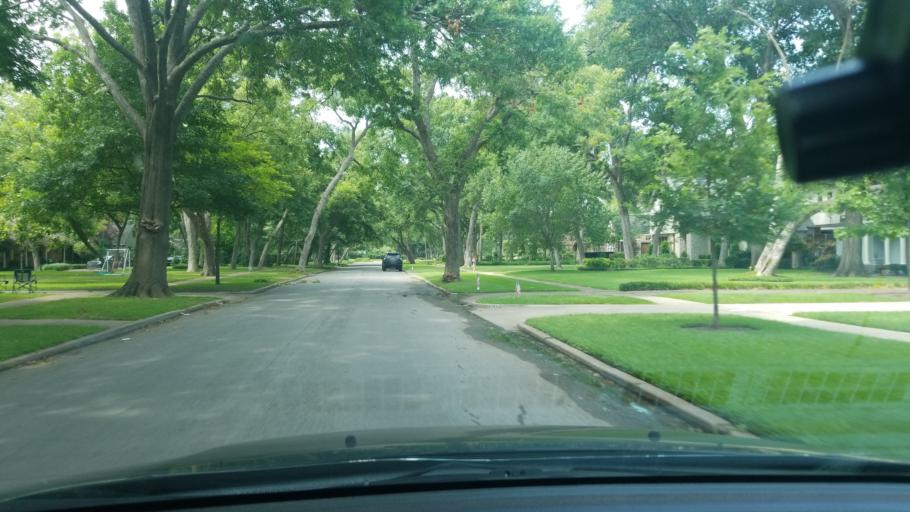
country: US
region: Texas
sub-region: Dallas County
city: Highland Park
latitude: 32.8145
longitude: -96.7146
